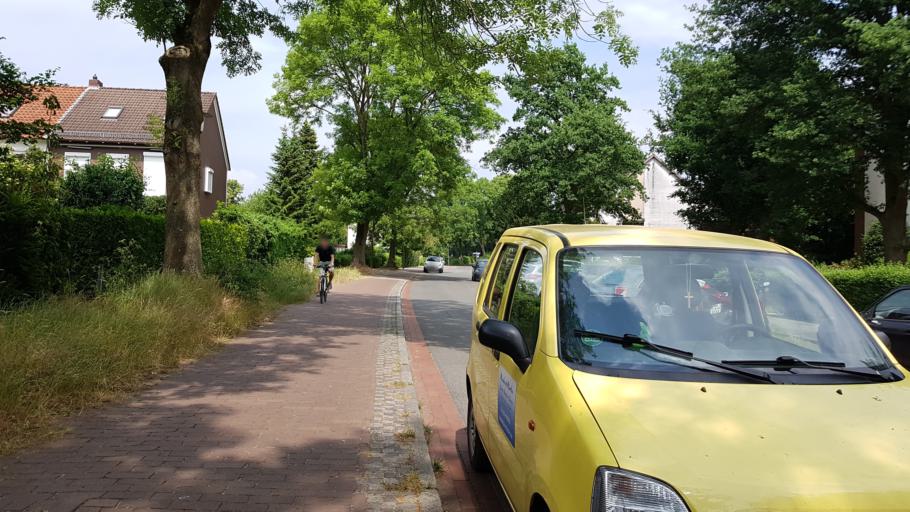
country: DE
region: Lower Saxony
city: Lilienthal
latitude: 53.1024
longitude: 8.8653
